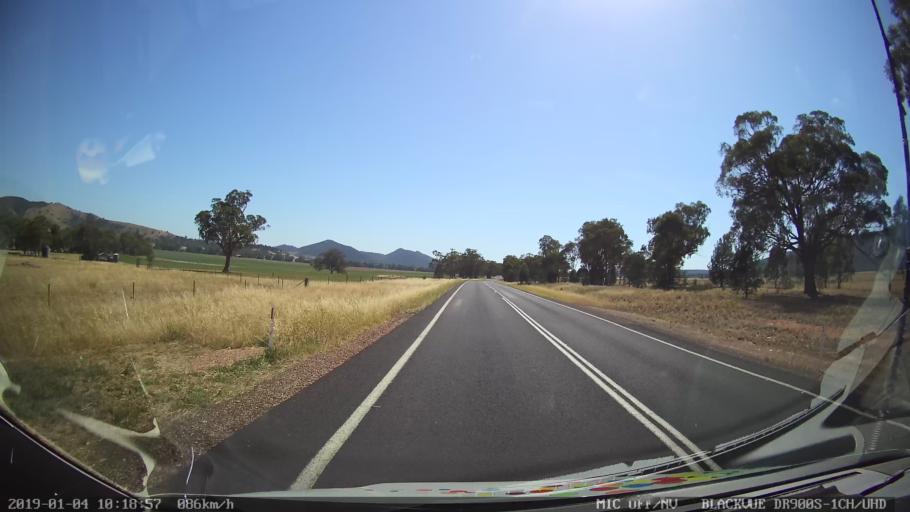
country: AU
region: New South Wales
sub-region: Cabonne
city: Canowindra
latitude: -33.3792
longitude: 148.4738
